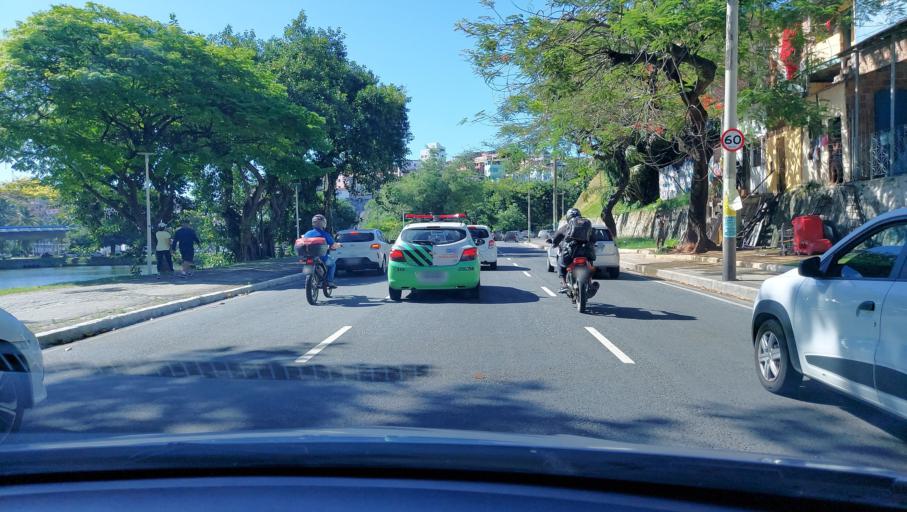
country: BR
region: Bahia
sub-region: Salvador
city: Salvador
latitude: -12.9872
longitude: -38.5089
